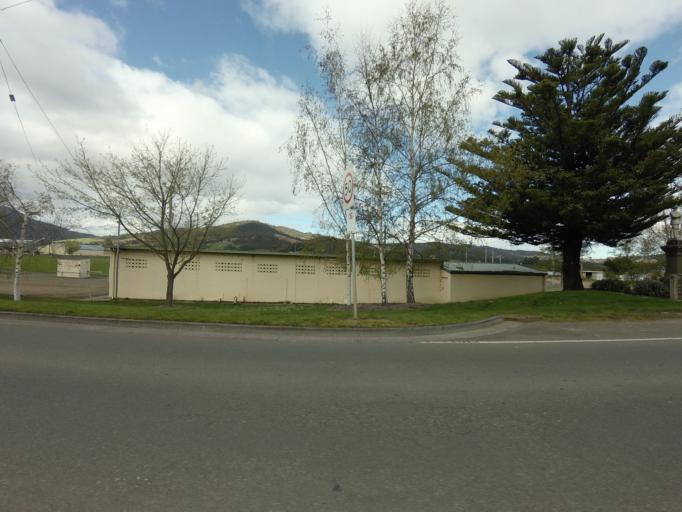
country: AU
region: Tasmania
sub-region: Huon Valley
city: Franklin
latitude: -43.0890
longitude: 147.0109
